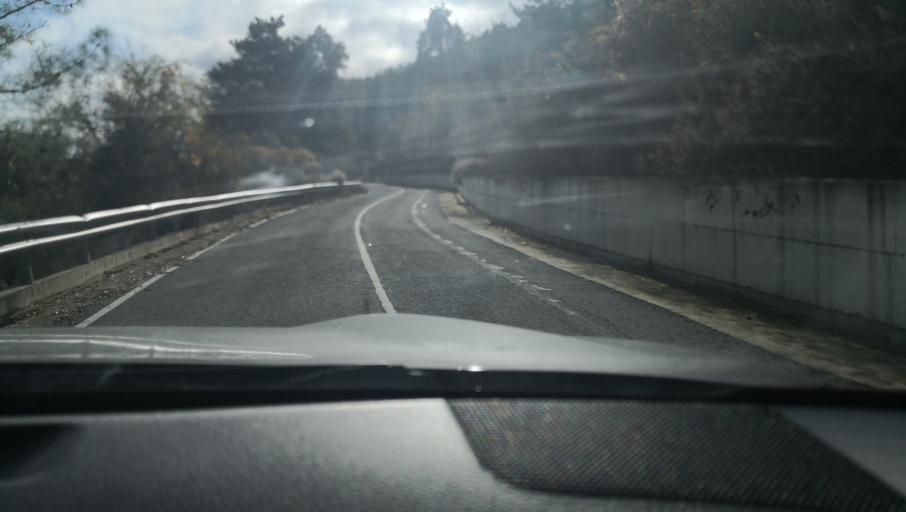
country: CY
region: Lefkosia
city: Lefka
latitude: 35.0169
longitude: 32.7279
